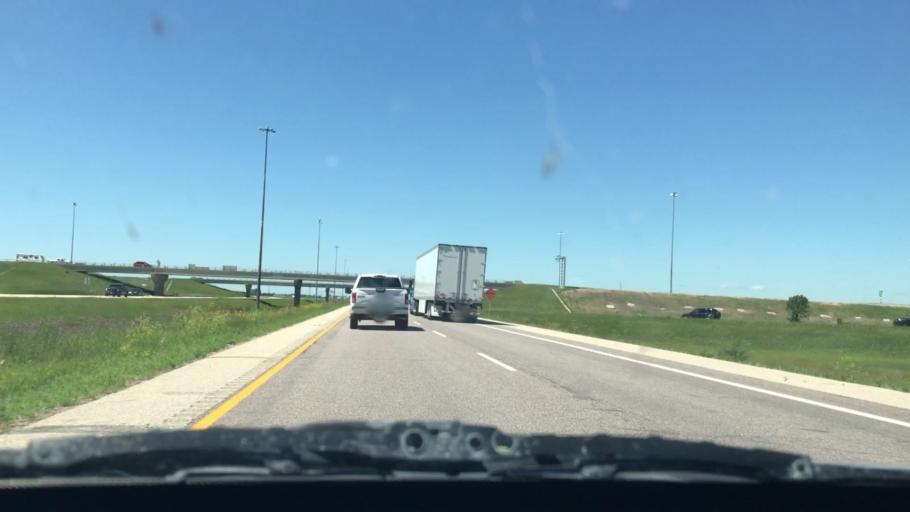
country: CA
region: Manitoba
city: Steinbach
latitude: 49.6998
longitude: -96.6424
